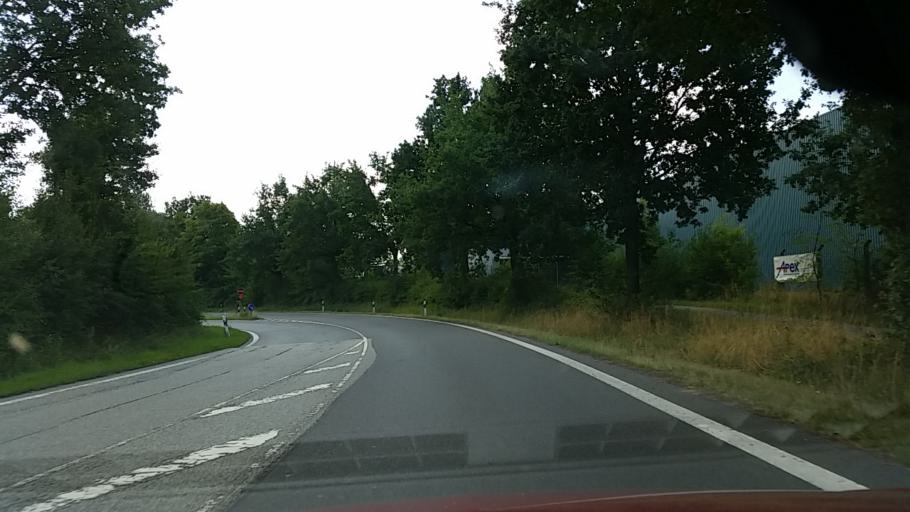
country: DE
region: Schleswig-Holstein
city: Reinbek
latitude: 53.5311
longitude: 10.2281
